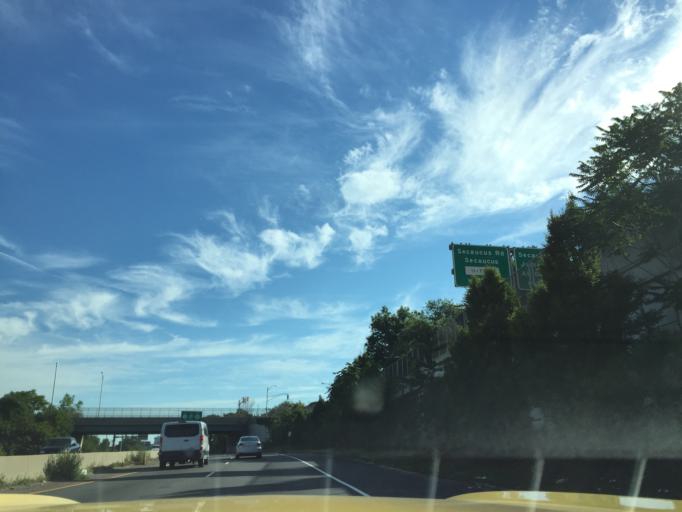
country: US
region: New Jersey
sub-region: Hudson County
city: Hoboken
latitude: 40.7589
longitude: -74.0521
